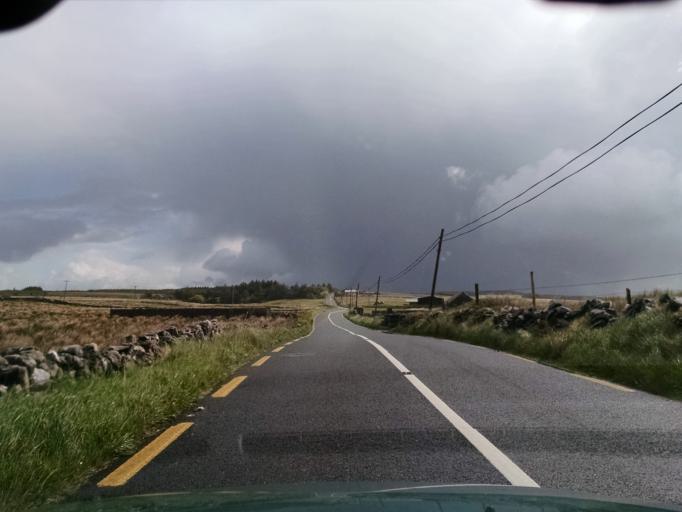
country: IE
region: Connaught
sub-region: County Galway
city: Bearna
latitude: 53.0484
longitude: -9.2346
